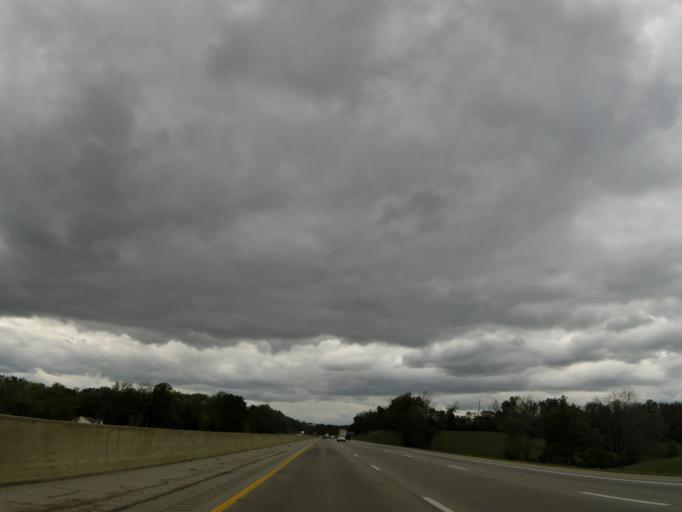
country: US
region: Kentucky
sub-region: Grant County
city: Crittenden
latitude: 38.7684
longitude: -84.6100
